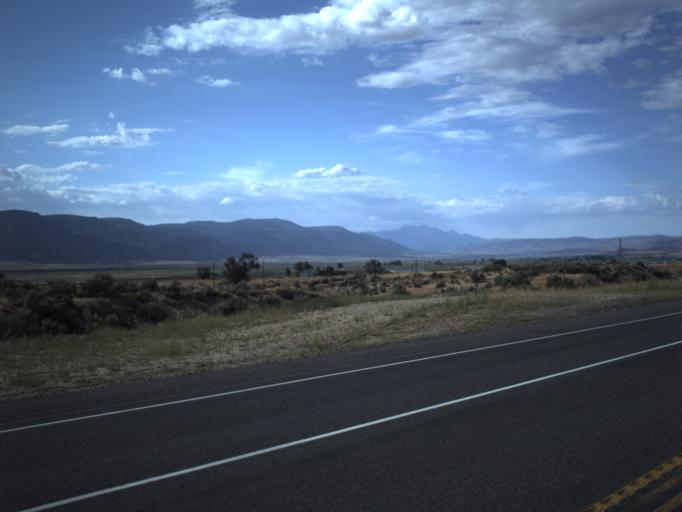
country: US
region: Utah
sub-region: Sanpete County
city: Ephraim
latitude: 39.4194
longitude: -111.5596
